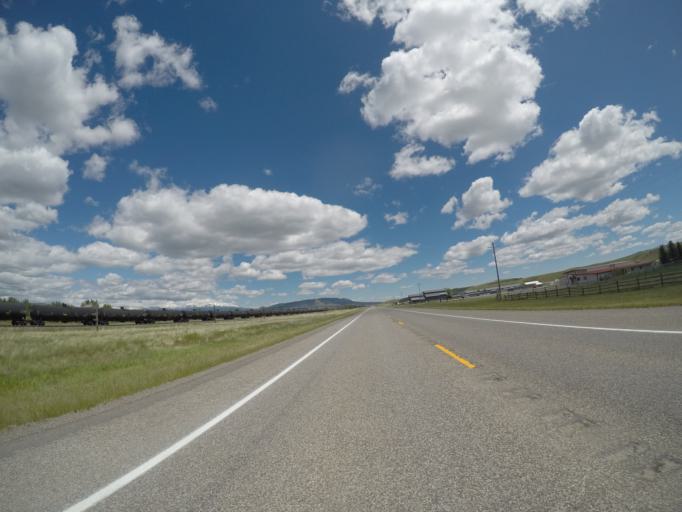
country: US
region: Montana
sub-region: Park County
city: Livingston
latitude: 45.6827
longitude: -110.5171
